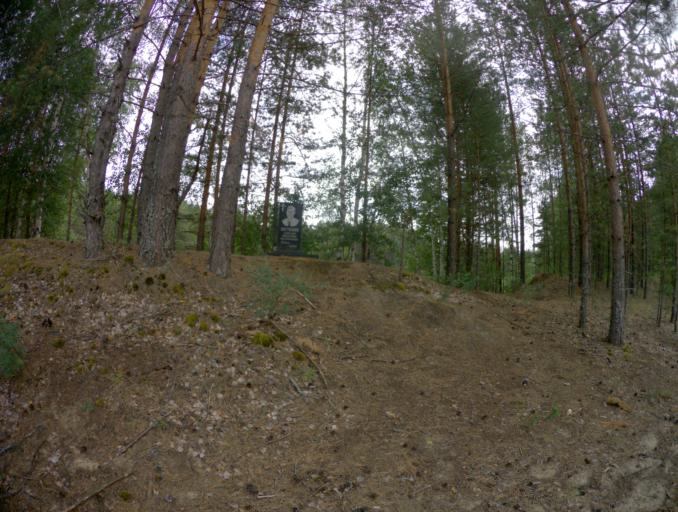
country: RU
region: Vladimir
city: Gorokhovets
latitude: 56.3039
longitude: 42.7384
